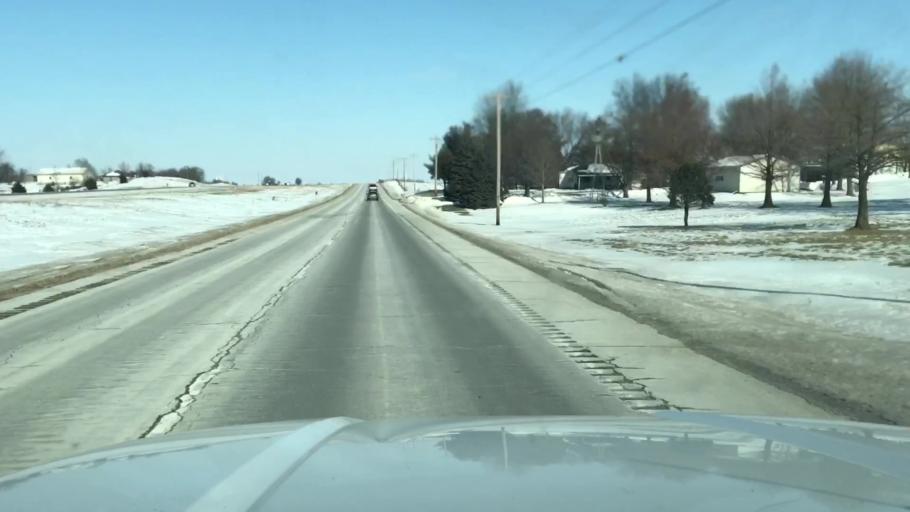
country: US
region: Missouri
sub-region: Andrew County
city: Savannah
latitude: 40.0008
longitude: -94.8797
